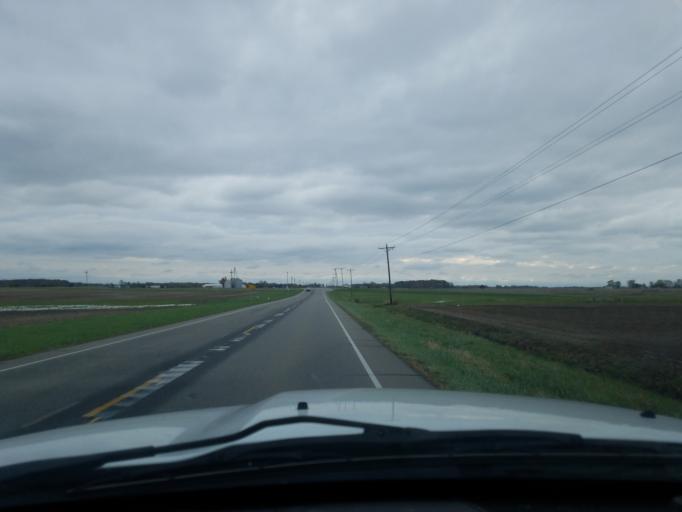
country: US
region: Indiana
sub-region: Bartholomew County
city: Hope
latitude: 39.2787
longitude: -85.7715
